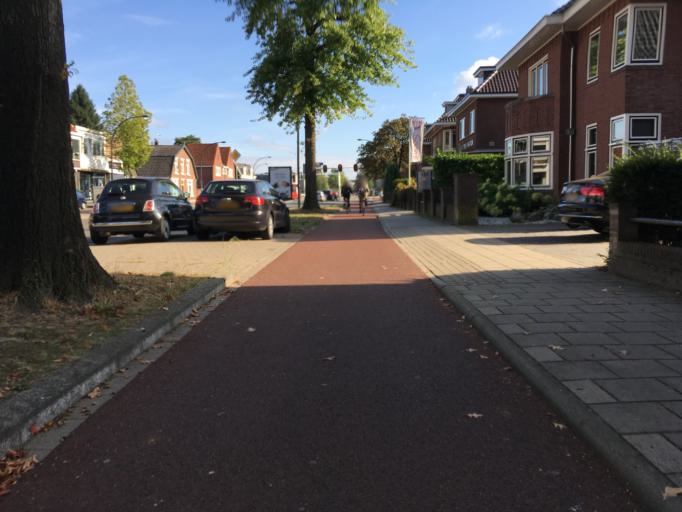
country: NL
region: Overijssel
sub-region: Gemeente Enschede
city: Enschede
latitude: 52.2269
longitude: 6.8789
